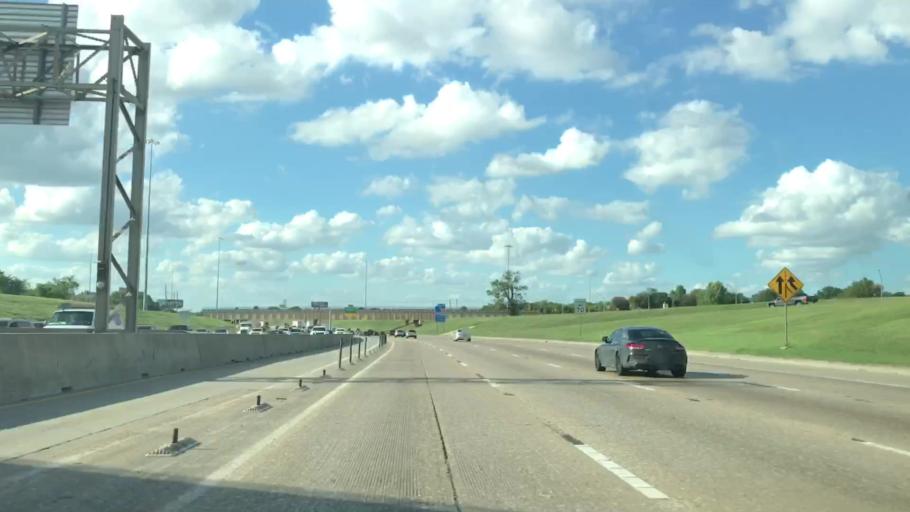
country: US
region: Texas
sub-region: Dallas County
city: Richardson
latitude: 32.8948
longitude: -96.7117
